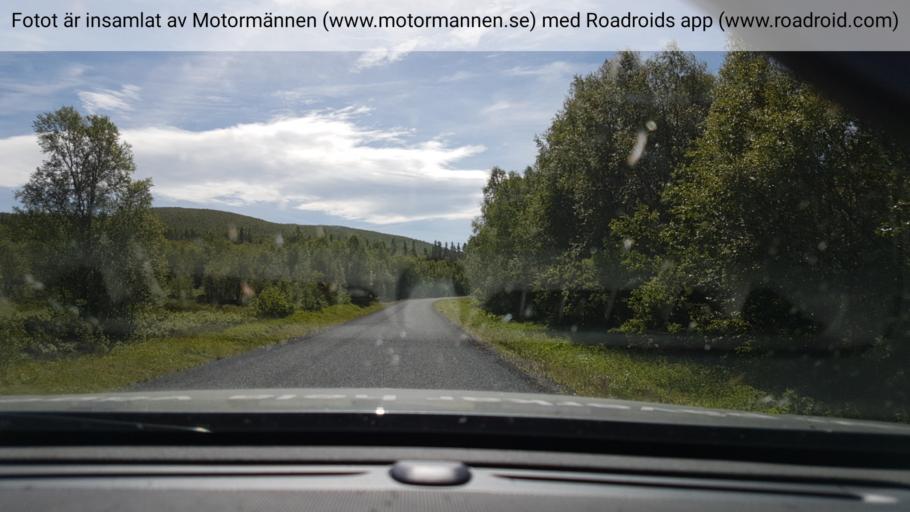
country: SE
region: Vaesterbotten
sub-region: Vilhelmina Kommun
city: Sjoberg
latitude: 65.3159
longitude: 15.2900
